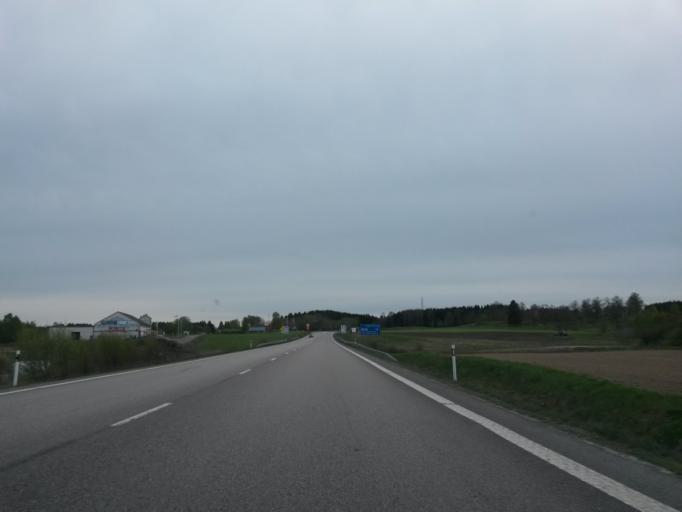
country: SE
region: Vaestra Goetaland
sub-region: Vargarda Kommun
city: Vargarda
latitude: 58.0551
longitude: 12.8174
